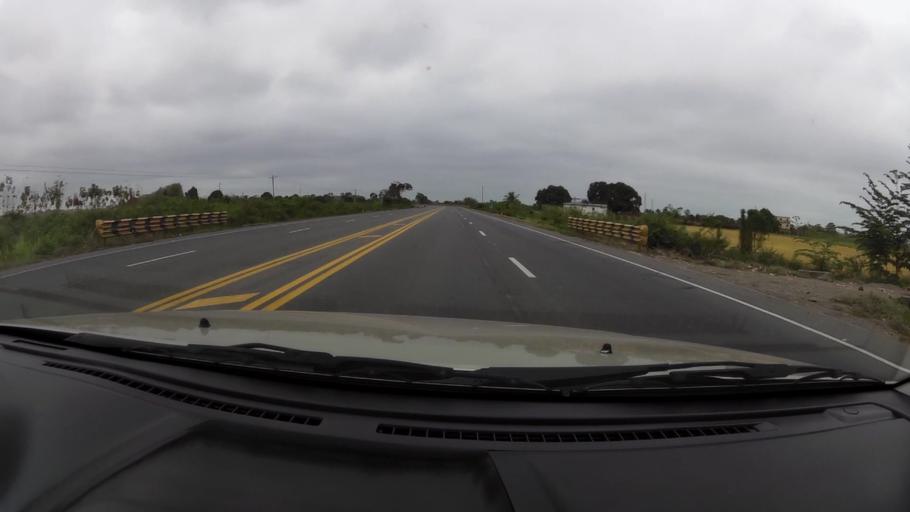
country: EC
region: Guayas
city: Naranjal
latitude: -2.4799
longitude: -79.6178
